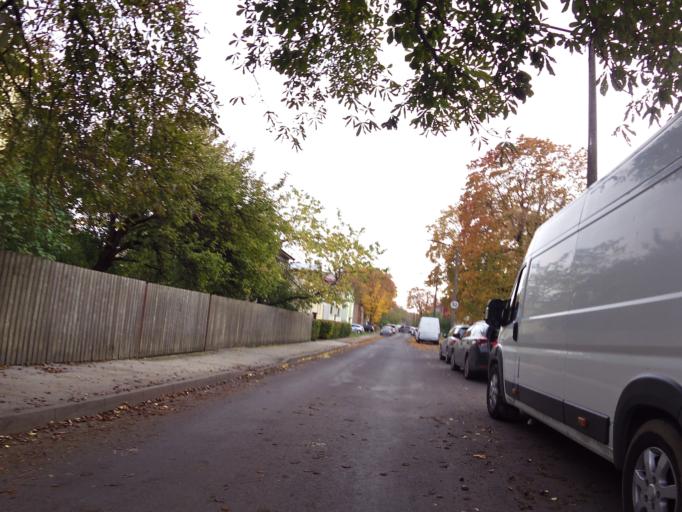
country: EE
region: Harju
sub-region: Tallinna linn
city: Tallinn
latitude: 59.4376
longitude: 24.7156
